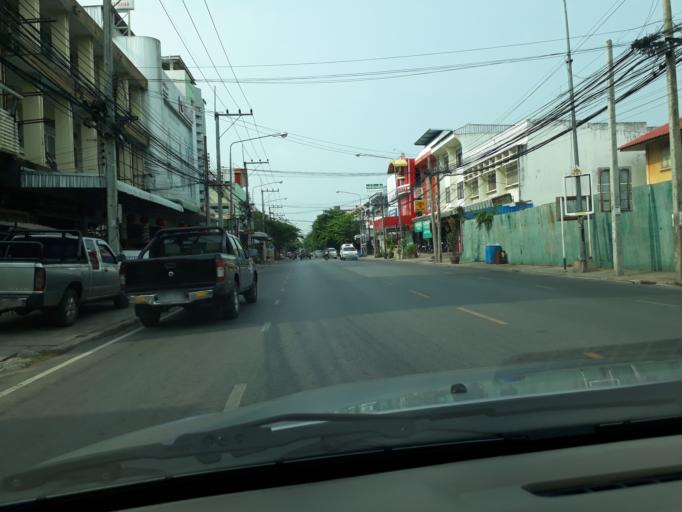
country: TH
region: Khon Kaen
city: Khon Kaen
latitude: 16.4382
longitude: 102.8348
